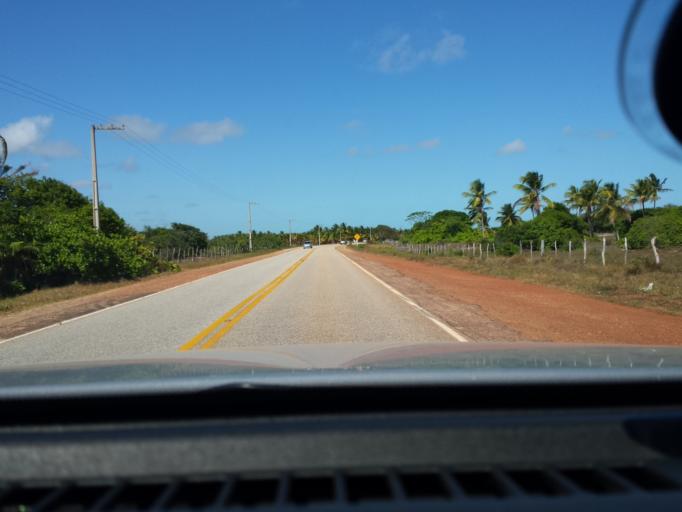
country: BR
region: Sergipe
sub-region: Estancia
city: Estancia
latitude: -11.2644
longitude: -37.2642
